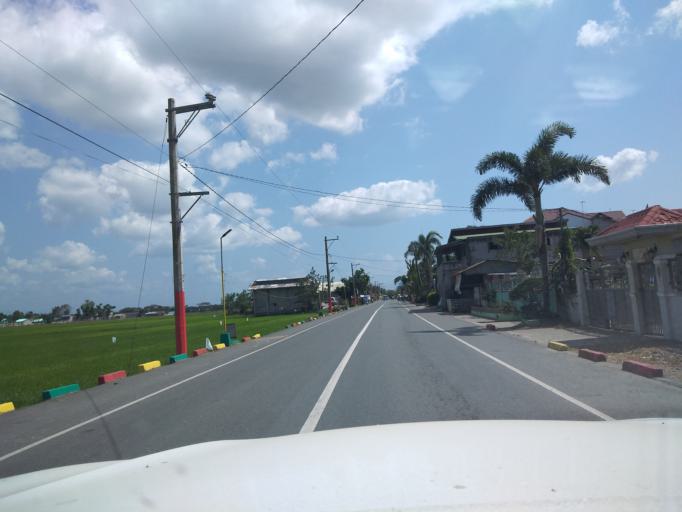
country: PH
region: Central Luzon
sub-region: Province of Pampanga
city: Bahay Pare
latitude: 15.0490
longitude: 120.8769
